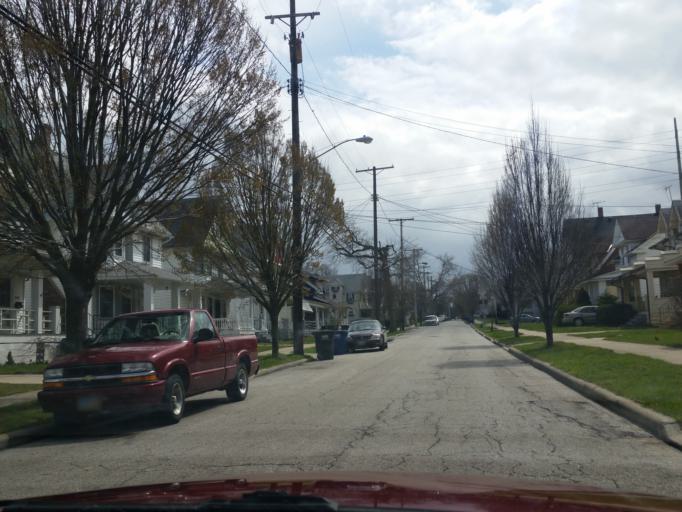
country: US
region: Ohio
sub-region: Cuyahoga County
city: Lakewood
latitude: 41.4877
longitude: -81.7740
